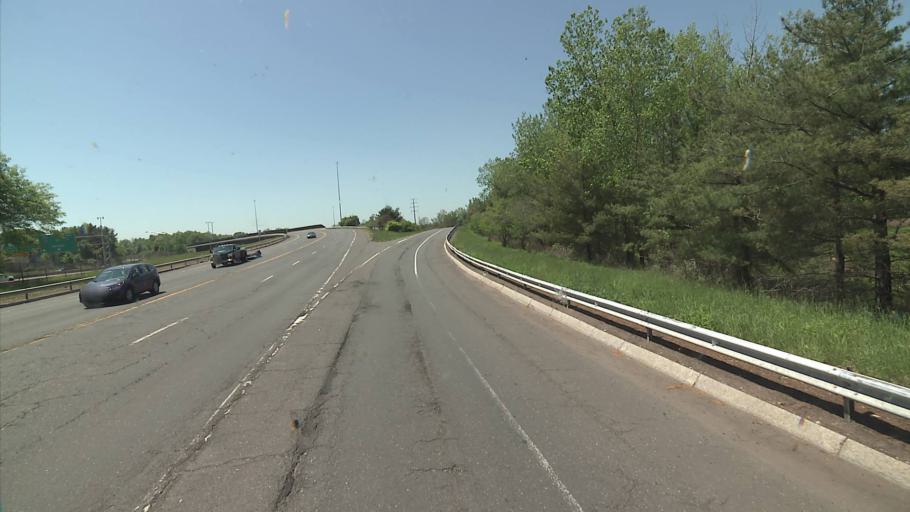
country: US
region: Connecticut
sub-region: Hartford County
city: East Hartford
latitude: 41.7672
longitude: -72.6238
